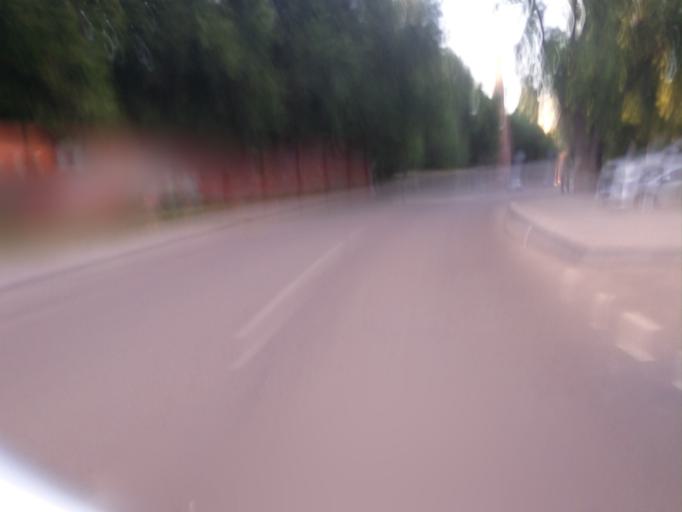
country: RU
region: Voronezj
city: Voronezh
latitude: 51.6493
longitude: 39.1674
